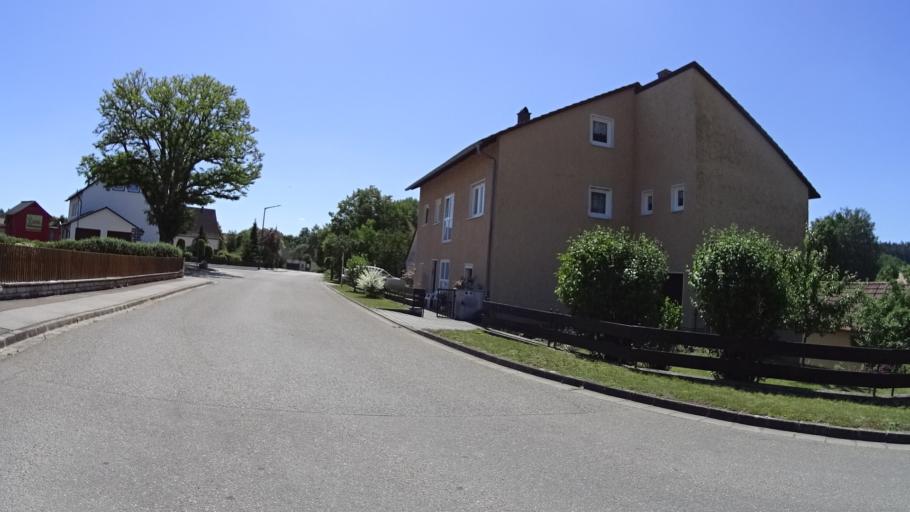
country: DE
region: Bavaria
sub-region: Regierungsbezirk Mittelfranken
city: Pleinfeld
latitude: 49.1053
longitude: 10.9522
